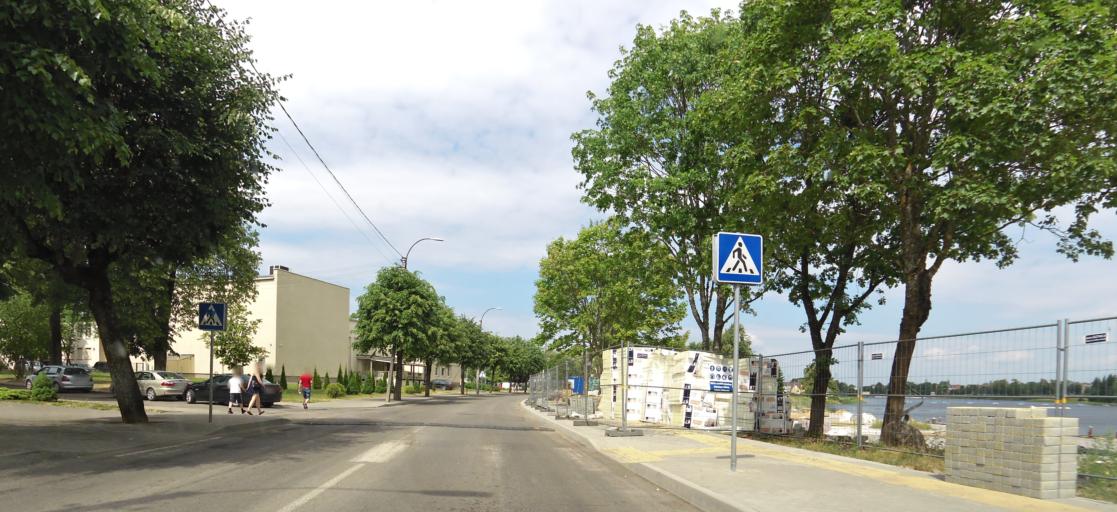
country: LT
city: Sirvintos
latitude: 55.0395
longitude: 24.9606
